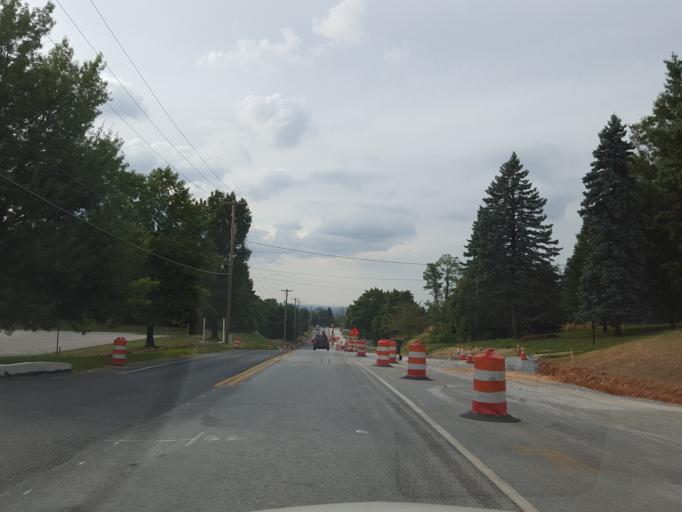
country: US
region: Pennsylvania
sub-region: York County
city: Stonybrook
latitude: 39.9547
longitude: -76.6517
